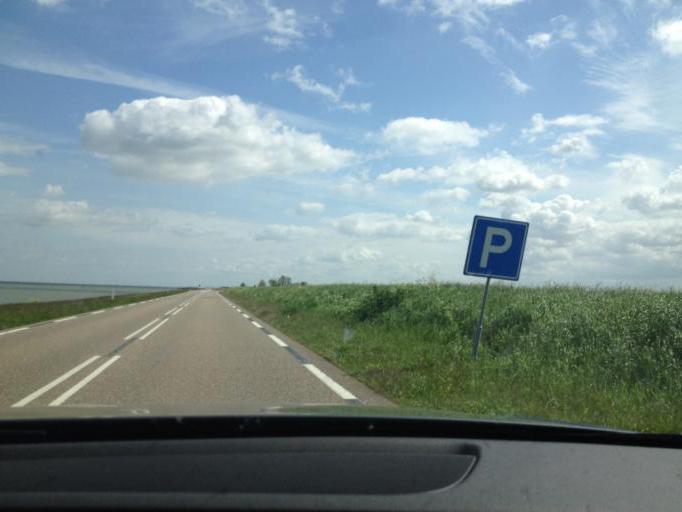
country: NL
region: Flevoland
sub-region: Gemeente Almere
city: Almere Stad
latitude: 52.4117
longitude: 5.1948
